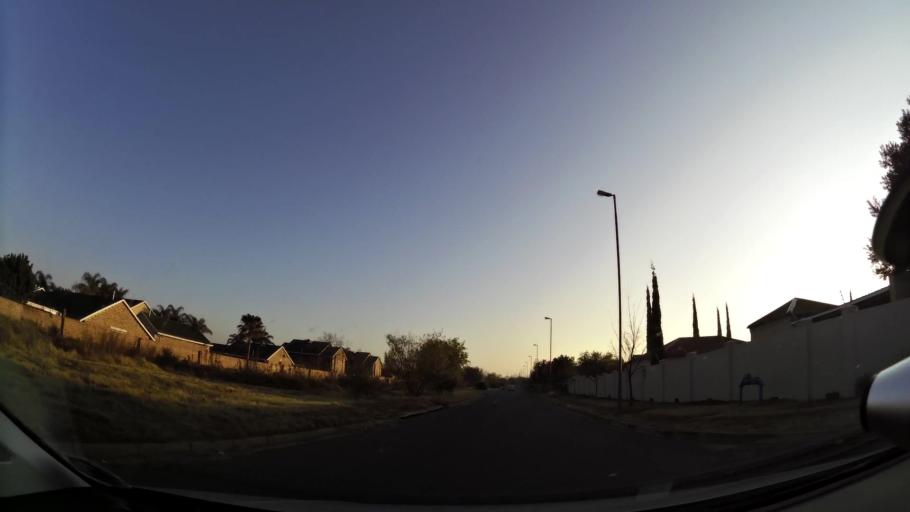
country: ZA
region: Orange Free State
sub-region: Mangaung Metropolitan Municipality
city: Bloemfontein
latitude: -29.1091
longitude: 26.1619
